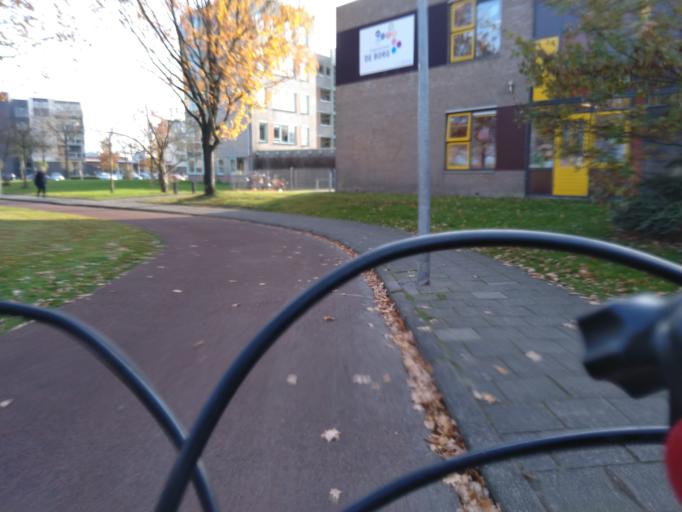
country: NL
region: Drenthe
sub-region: Gemeente Assen
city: Assen
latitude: 53.0181
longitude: 6.5828
